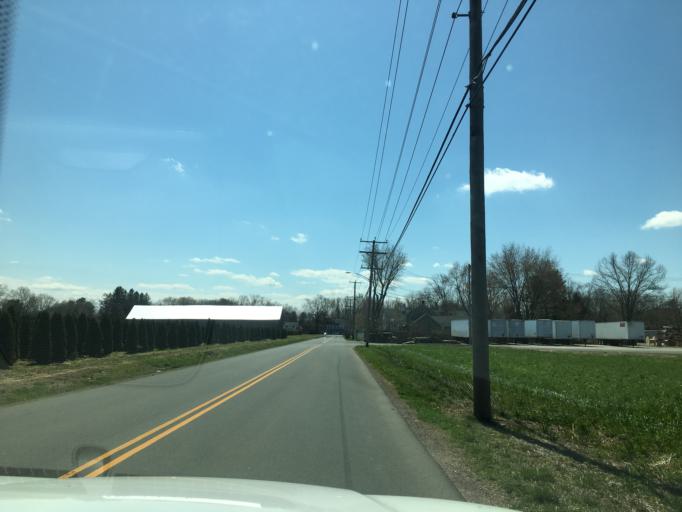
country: US
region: Connecticut
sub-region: Hartford County
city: Hazardville
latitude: 41.9892
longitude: -72.5285
